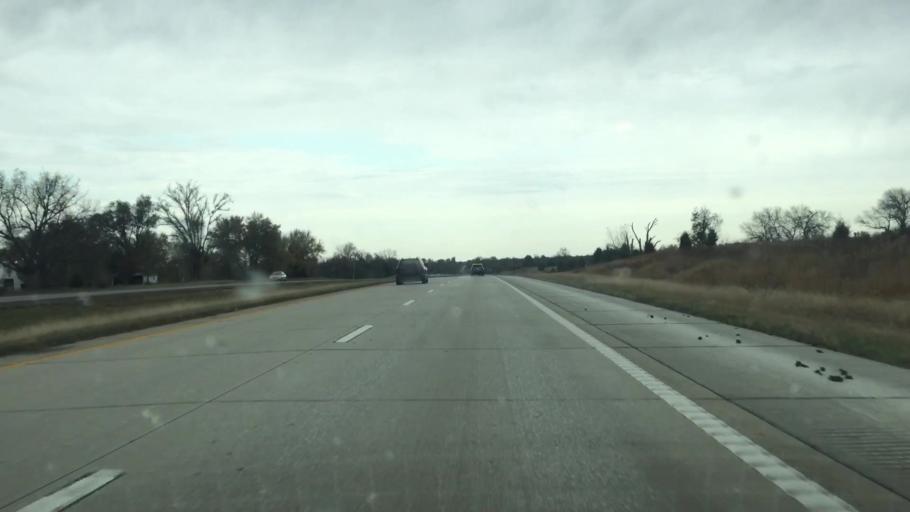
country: US
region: Missouri
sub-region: Saint Clair County
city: Osceola
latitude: 38.1680
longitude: -93.7220
